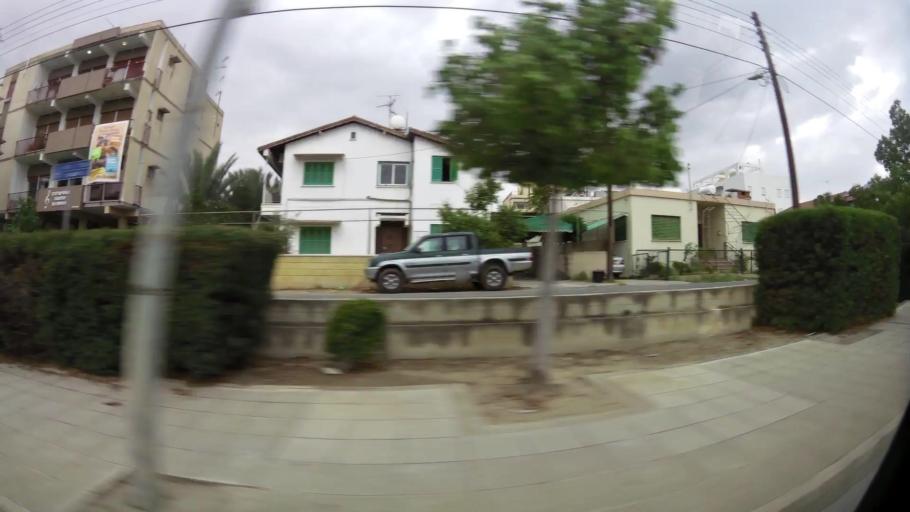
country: CY
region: Lefkosia
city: Nicosia
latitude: 35.1440
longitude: 33.3592
